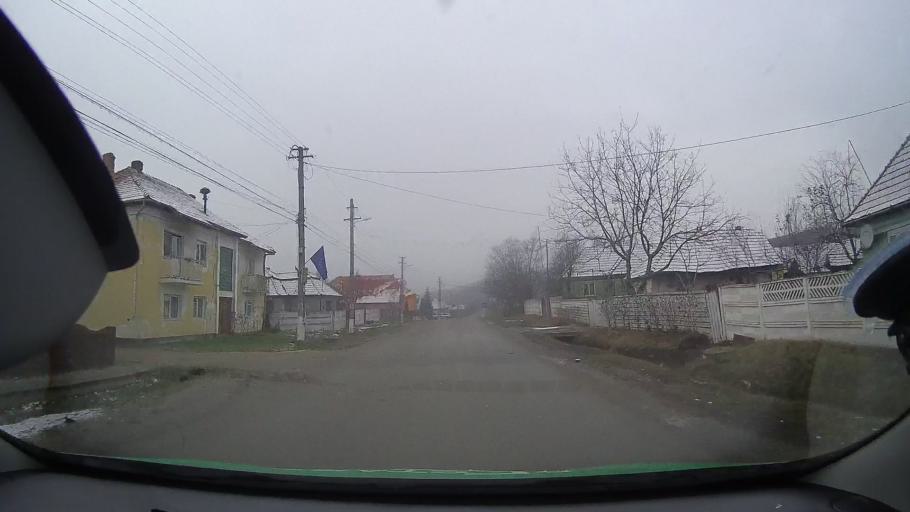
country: RO
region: Alba
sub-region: Comuna Farau
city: Farau
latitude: 46.3400
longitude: 23.9983
